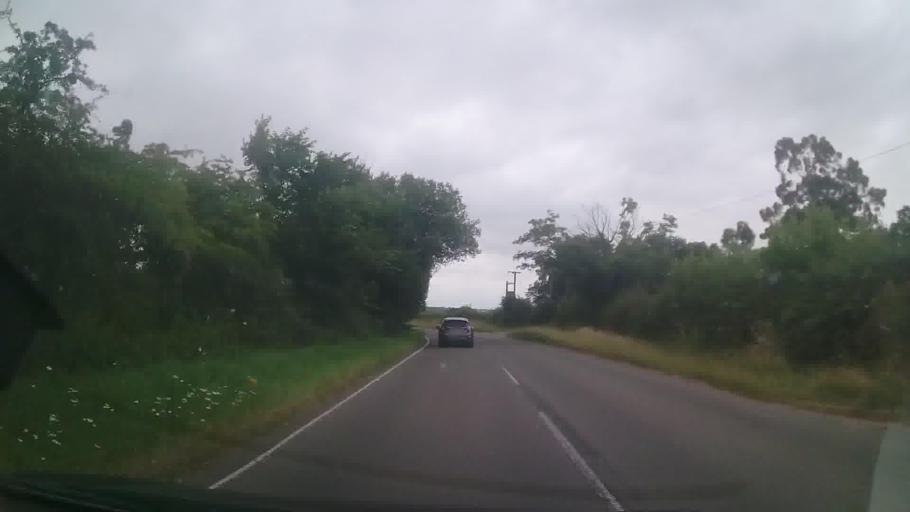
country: GB
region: England
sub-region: Leicestershire
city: Desford
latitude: 52.6528
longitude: -1.2921
